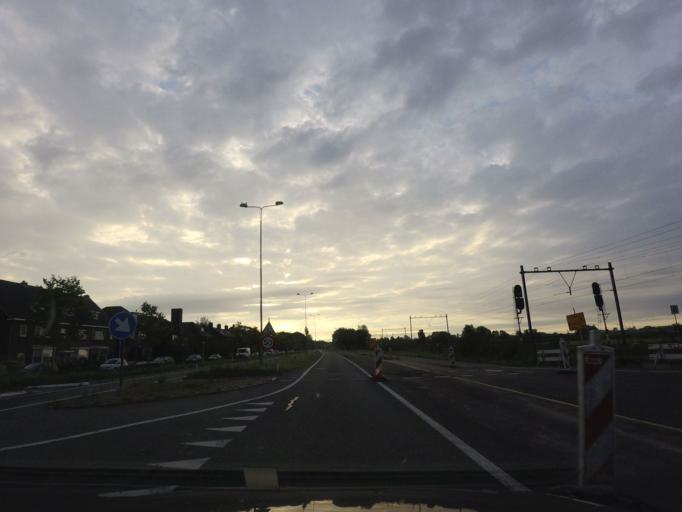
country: NL
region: North Holland
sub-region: Gemeente Zaanstad
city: Zaanstad
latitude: 52.4910
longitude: 4.7859
